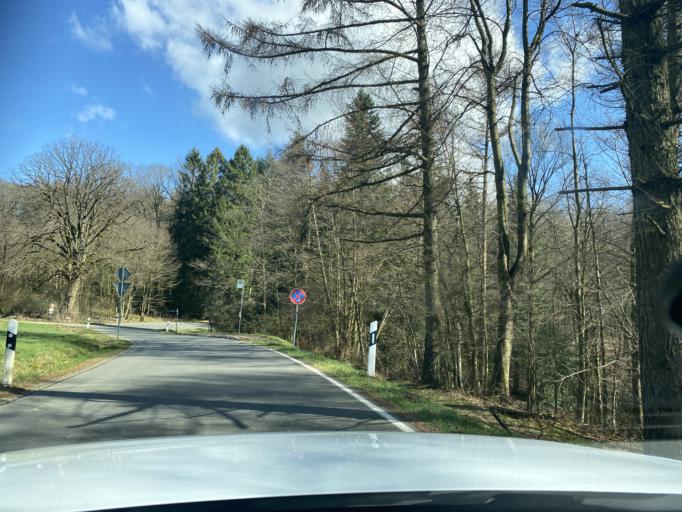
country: DE
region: North Rhine-Westphalia
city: Wipperfurth
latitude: 51.1496
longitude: 7.3924
